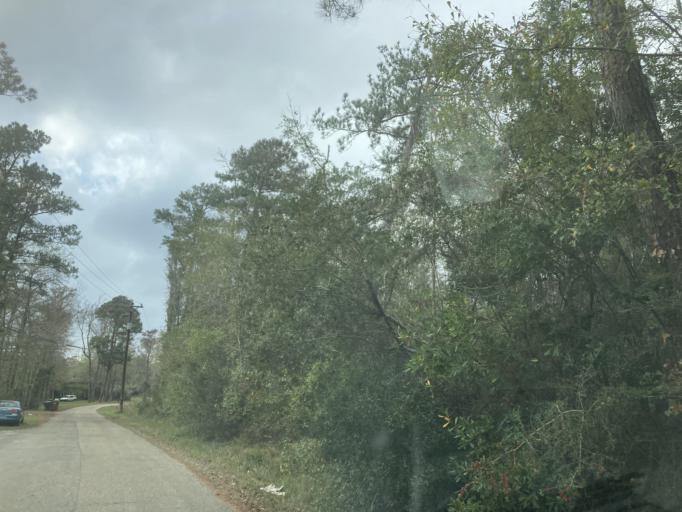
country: US
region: Mississippi
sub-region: Harrison County
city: West Gulfport
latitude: 30.4770
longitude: -89.0166
